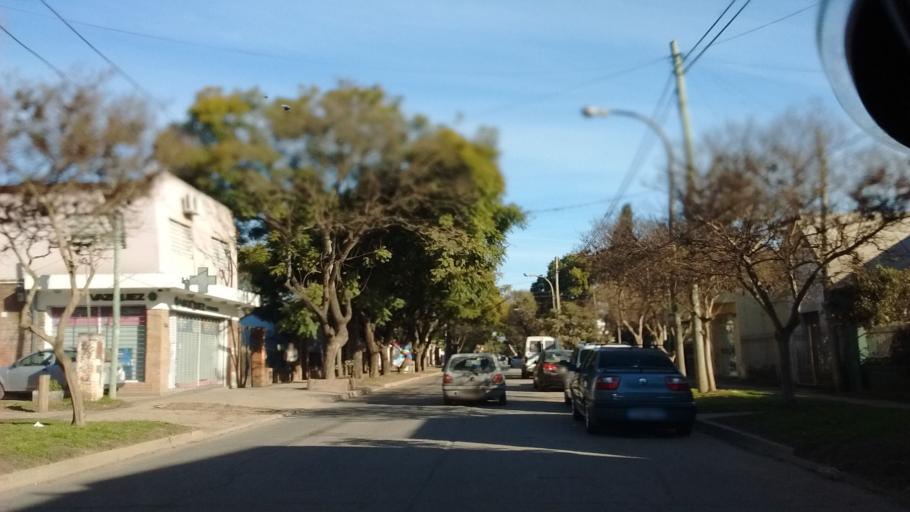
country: AR
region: Santa Fe
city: Funes
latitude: -32.9146
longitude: -60.8131
